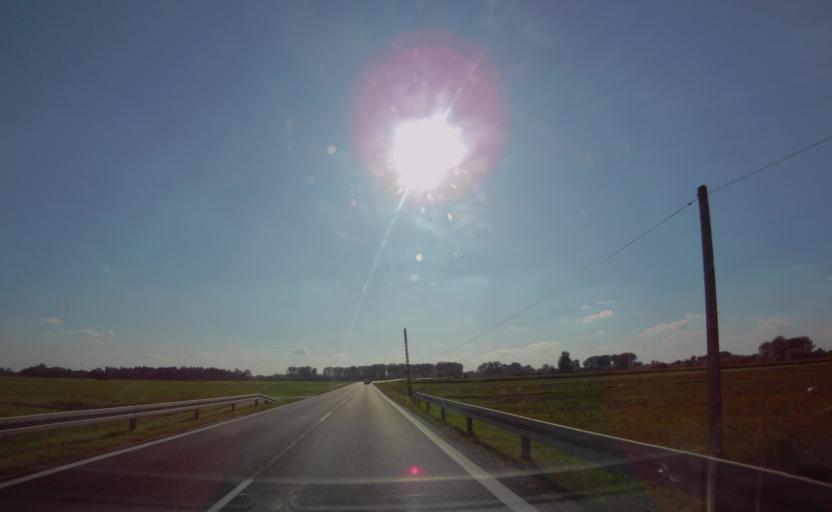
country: PL
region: Subcarpathian Voivodeship
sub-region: Powiat lezajski
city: Kurylowka
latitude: 50.2946
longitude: 22.4520
